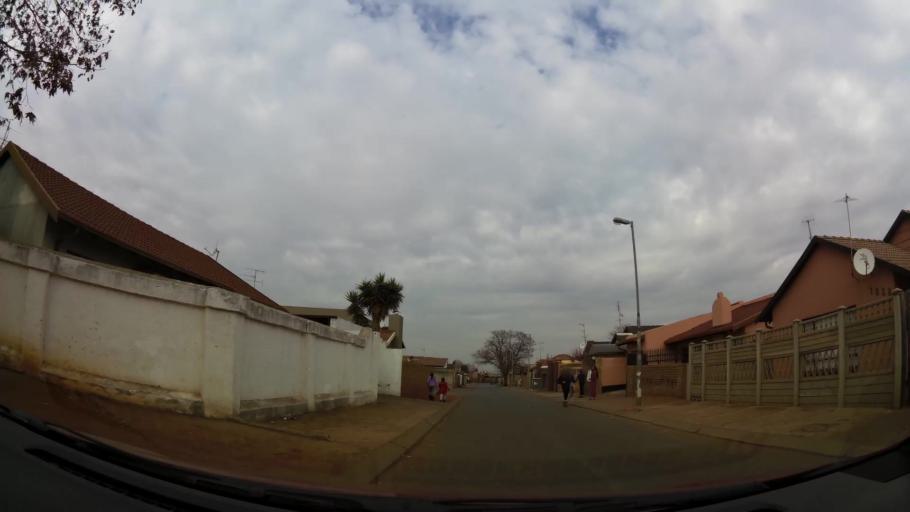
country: ZA
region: Gauteng
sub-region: City of Johannesburg Metropolitan Municipality
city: Soweto
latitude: -26.2692
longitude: 27.8302
